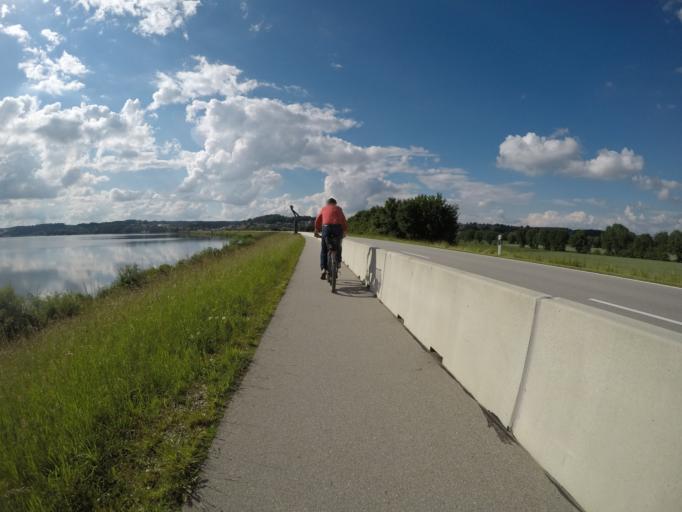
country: DE
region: Bavaria
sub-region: Lower Bavaria
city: Reisbach
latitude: 48.5660
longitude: 12.5971
